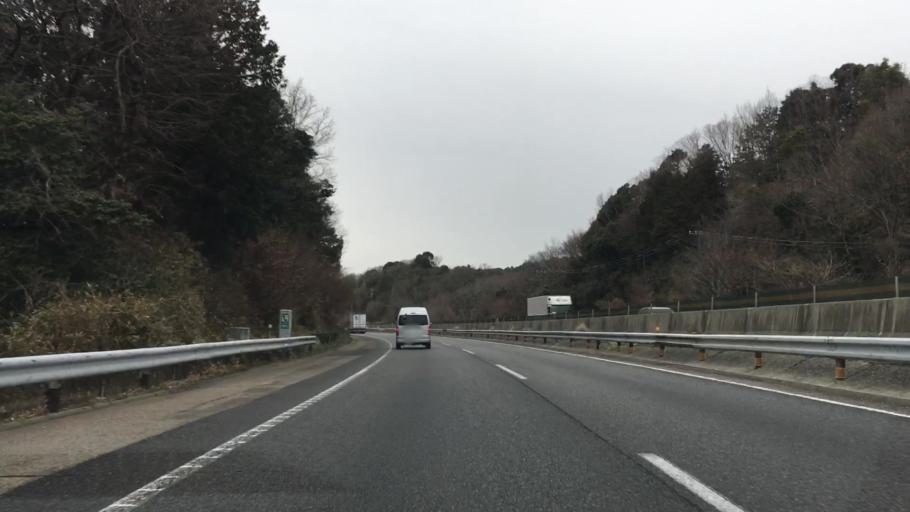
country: JP
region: Aichi
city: Gamagori
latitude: 34.9011
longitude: 137.2552
